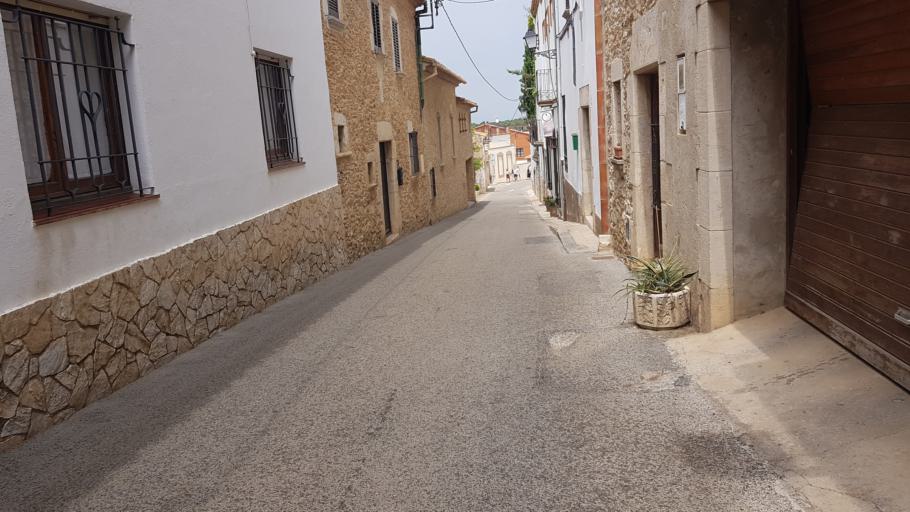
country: ES
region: Catalonia
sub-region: Provincia de Girona
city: Begur
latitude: 41.9557
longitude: 3.2068
